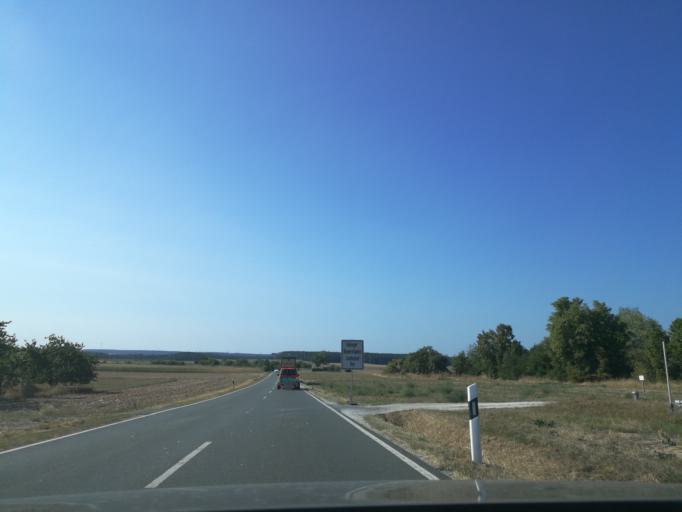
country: DE
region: Bavaria
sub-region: Regierungsbezirk Mittelfranken
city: Cadolzburg
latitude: 49.4516
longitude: 10.8491
